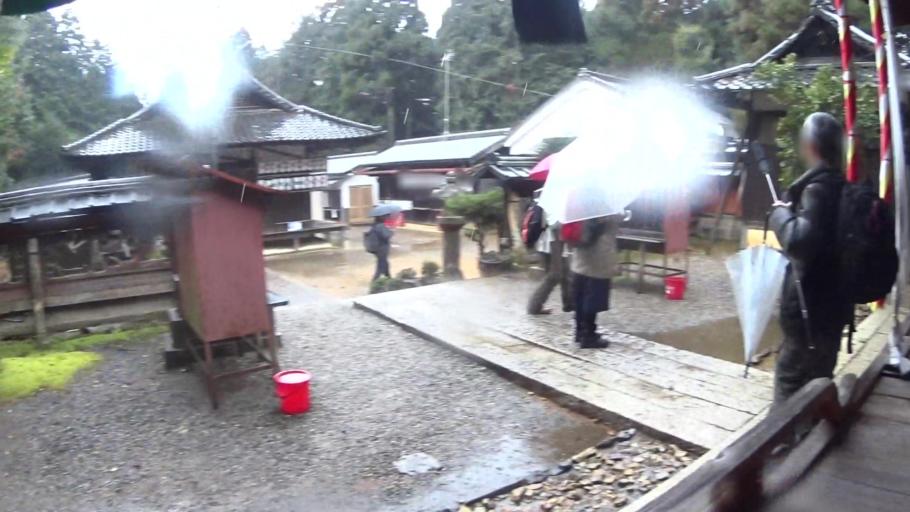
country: JP
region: Kyoto
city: Uji
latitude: 34.9556
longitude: 135.8215
